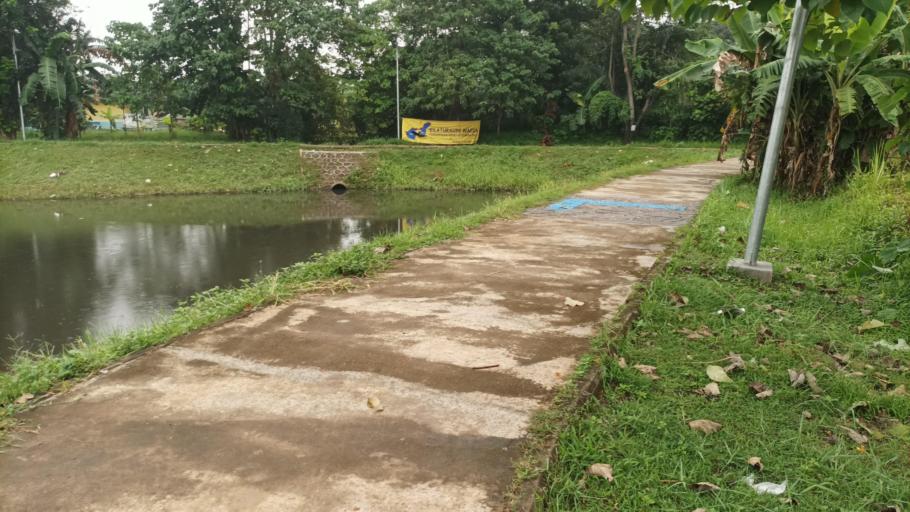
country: ID
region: West Java
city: Cileungsir
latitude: -6.3906
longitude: 106.9145
